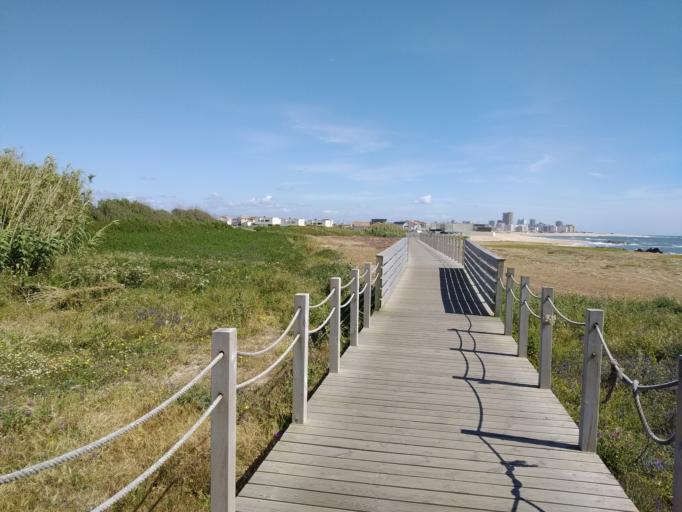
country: PT
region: Porto
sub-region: Povoa de Varzim
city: Aver-o-Mar
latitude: 41.4107
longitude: -8.7838
